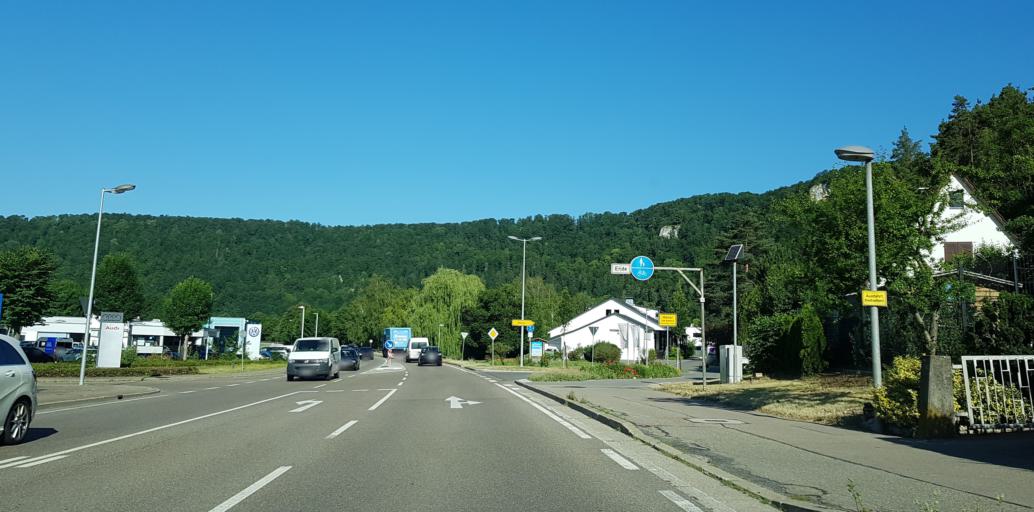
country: DE
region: Baden-Wuerttemberg
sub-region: Tuebingen Region
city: Blaubeuren
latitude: 48.4039
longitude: 9.7784
